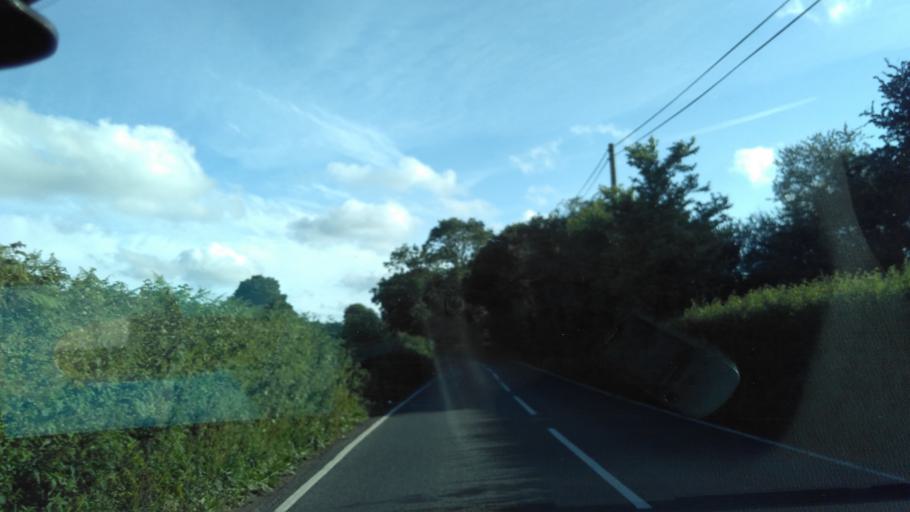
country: GB
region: England
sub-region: Kent
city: Kennington
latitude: 51.2346
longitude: 0.8724
